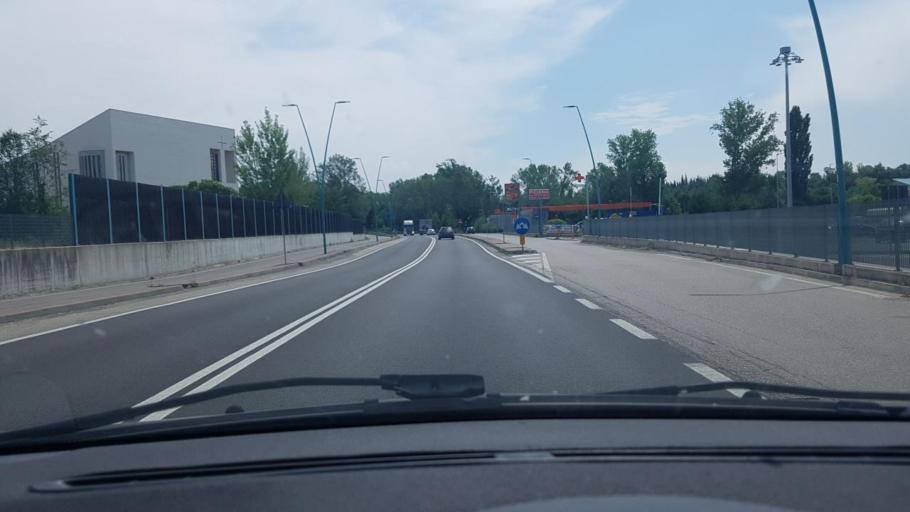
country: IT
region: Veneto
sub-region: Provincia di Verona
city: Peschiera del Garda
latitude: 45.4347
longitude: 10.6817
